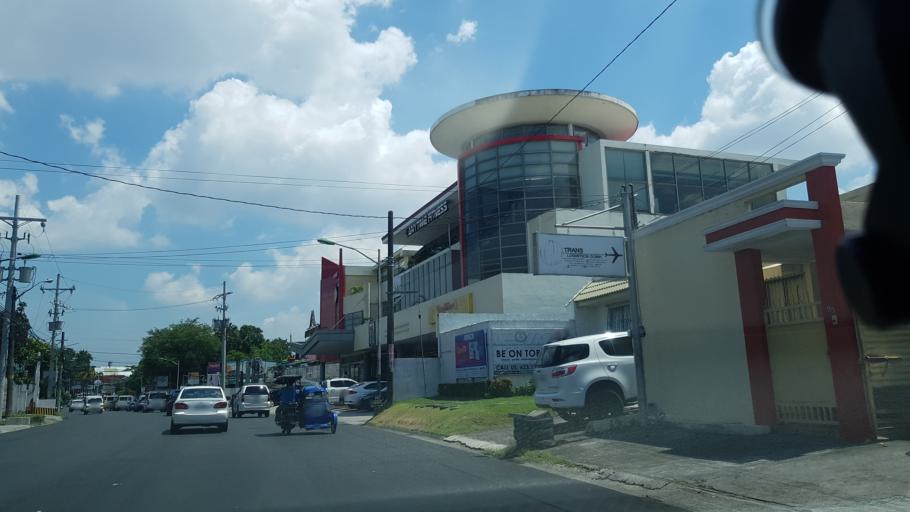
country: PH
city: Sambayanihan People's Village
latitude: 14.4463
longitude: 121.0208
